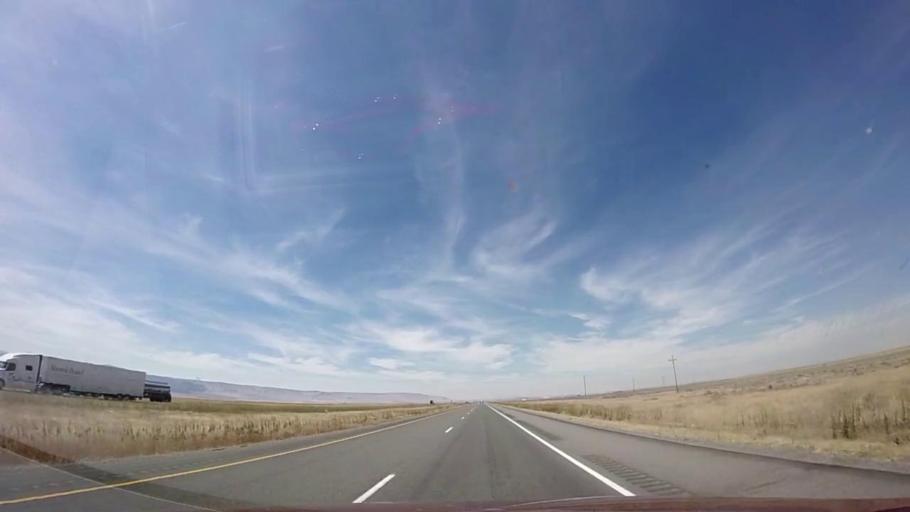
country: US
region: Idaho
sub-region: Minidoka County
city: Rupert
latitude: 42.3595
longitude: -113.2537
